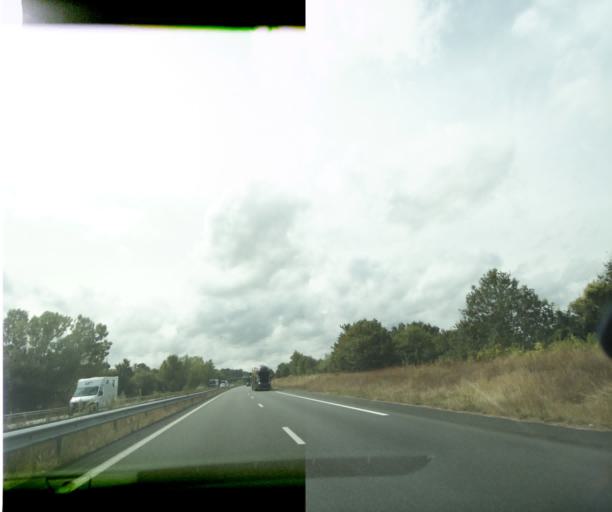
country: FR
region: Poitou-Charentes
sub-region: Departement de la Charente-Maritime
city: Saint-Genis-de-Saintonge
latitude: 45.4959
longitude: -0.6137
